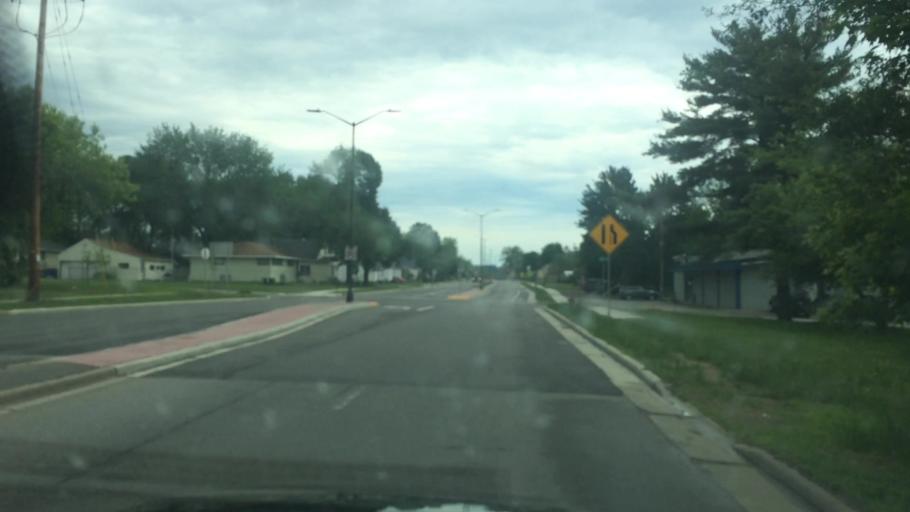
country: US
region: Wisconsin
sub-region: Marathon County
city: Wausau
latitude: 44.9483
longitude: -89.6545
